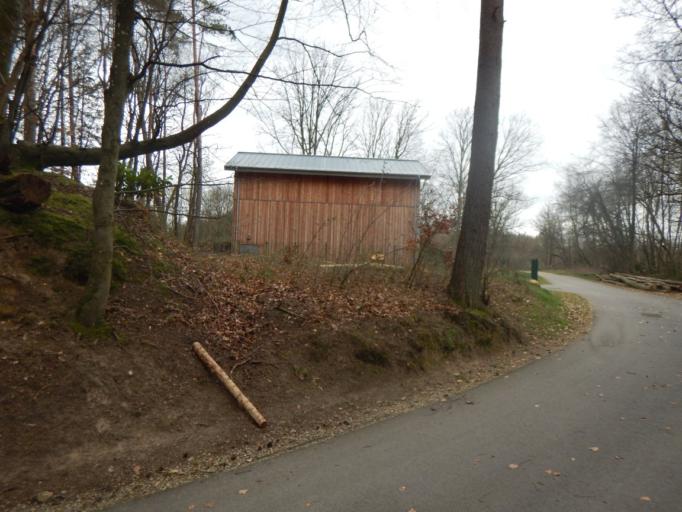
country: LU
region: Luxembourg
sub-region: Canton de Mersch
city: Lorentzweiler
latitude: 49.7012
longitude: 6.1631
